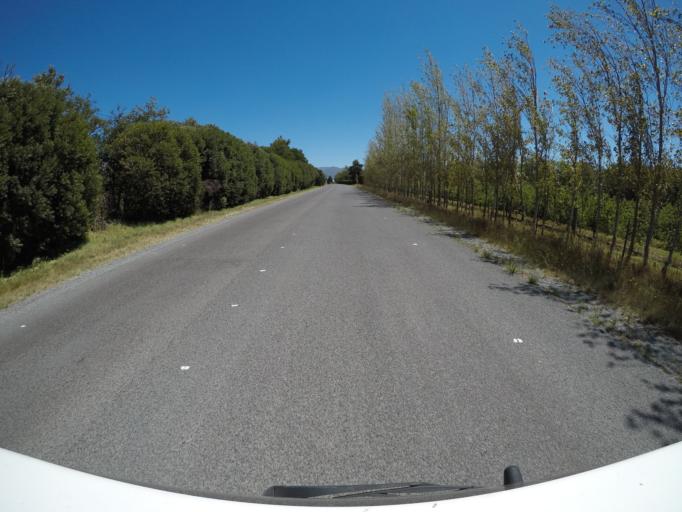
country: ZA
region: Western Cape
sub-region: Overberg District Municipality
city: Grabouw
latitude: -34.1837
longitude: 19.0382
